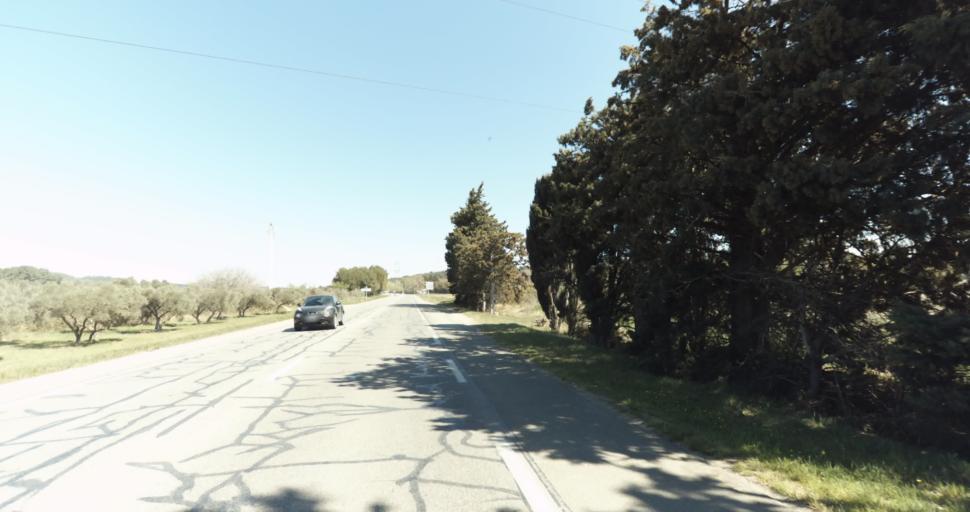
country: FR
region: Provence-Alpes-Cote d'Azur
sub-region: Departement des Bouches-du-Rhone
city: Pelissanne
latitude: 43.6380
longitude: 5.1786
